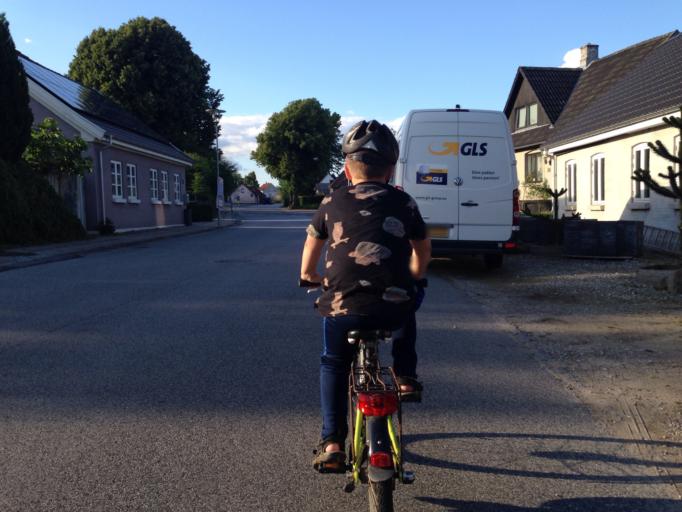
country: DK
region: South Denmark
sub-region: Middelfart Kommune
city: Norre Aby
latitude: 55.4876
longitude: 9.9085
